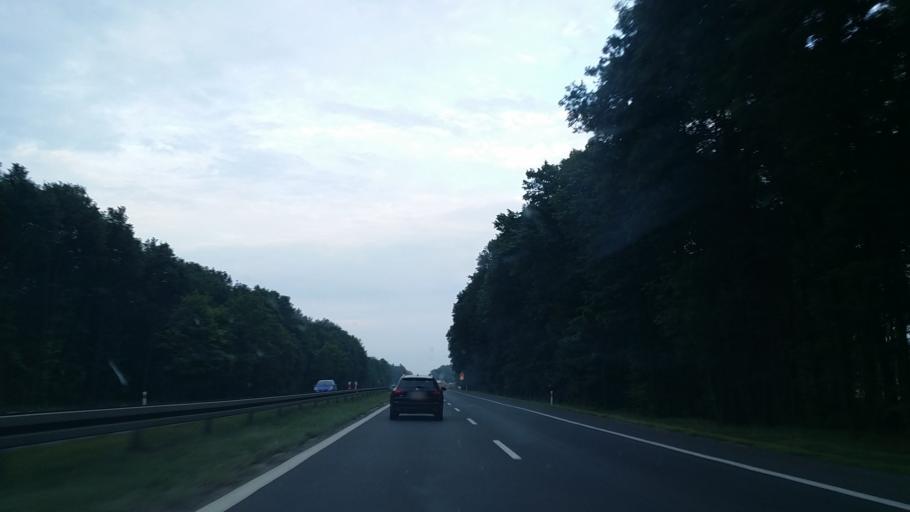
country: PL
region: Lower Silesian Voivodeship
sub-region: Powiat lubinski
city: Lubin
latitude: 51.4423
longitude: 16.1442
